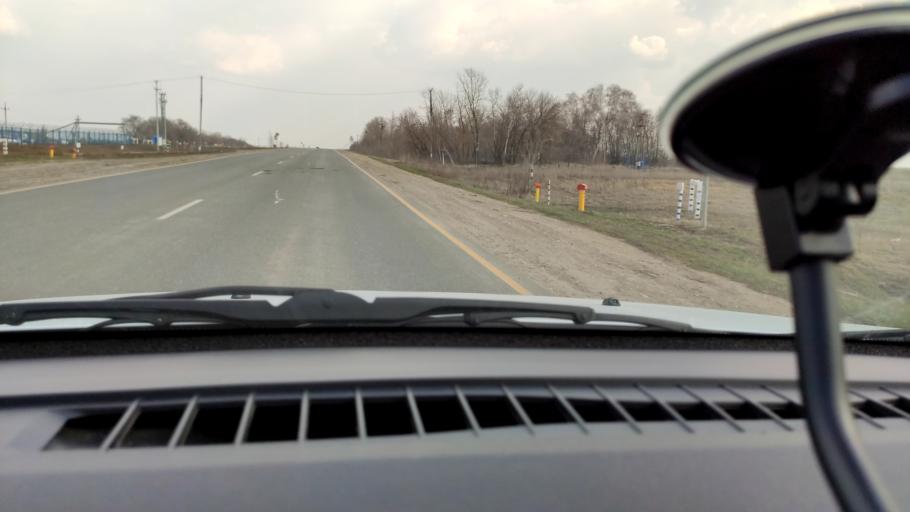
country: RU
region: Samara
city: Dubovyy Umet
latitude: 53.0817
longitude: 50.3463
